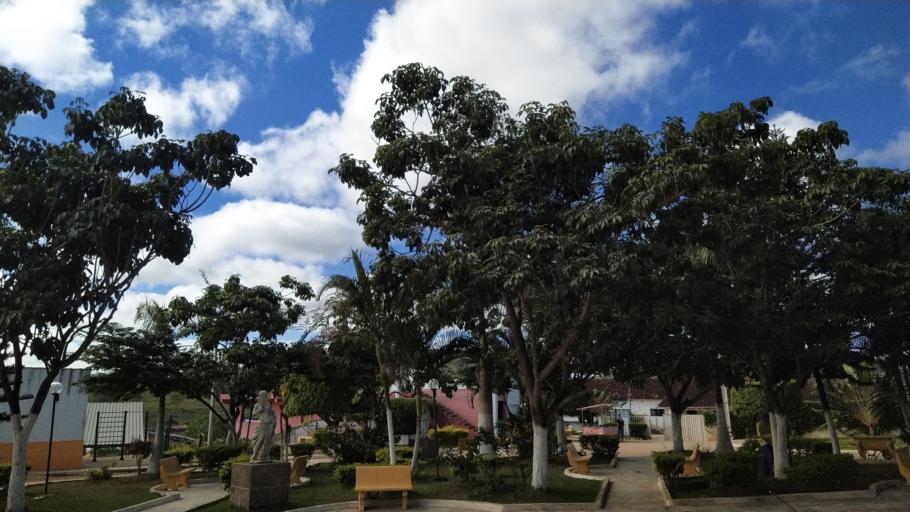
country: BR
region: Bahia
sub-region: Itanhem
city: Itanhem
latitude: -16.7424
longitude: -40.4233
